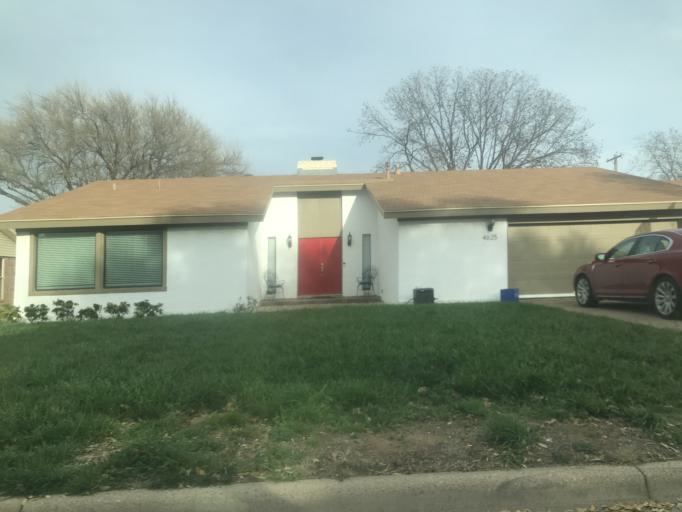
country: US
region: Texas
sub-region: Taylor County
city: Abilene
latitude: 32.3940
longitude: -99.7705
